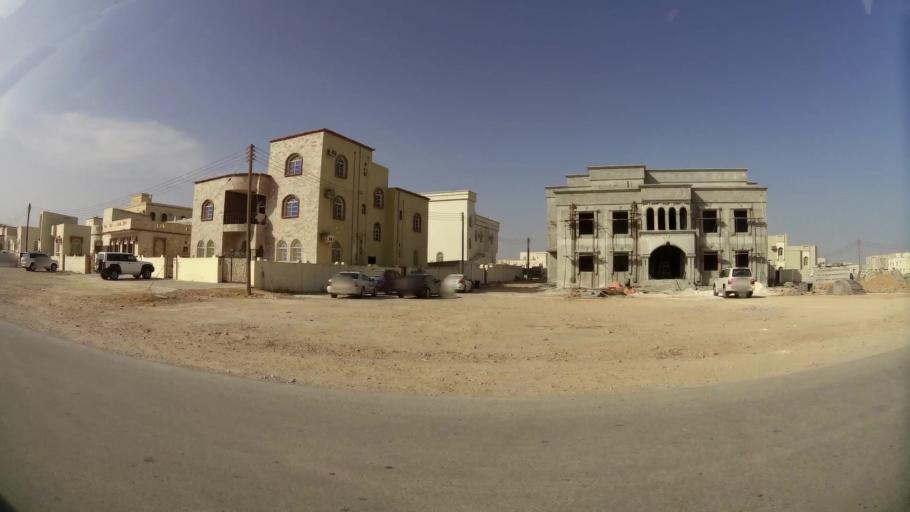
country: OM
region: Zufar
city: Salalah
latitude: 17.0068
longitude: 54.0163
